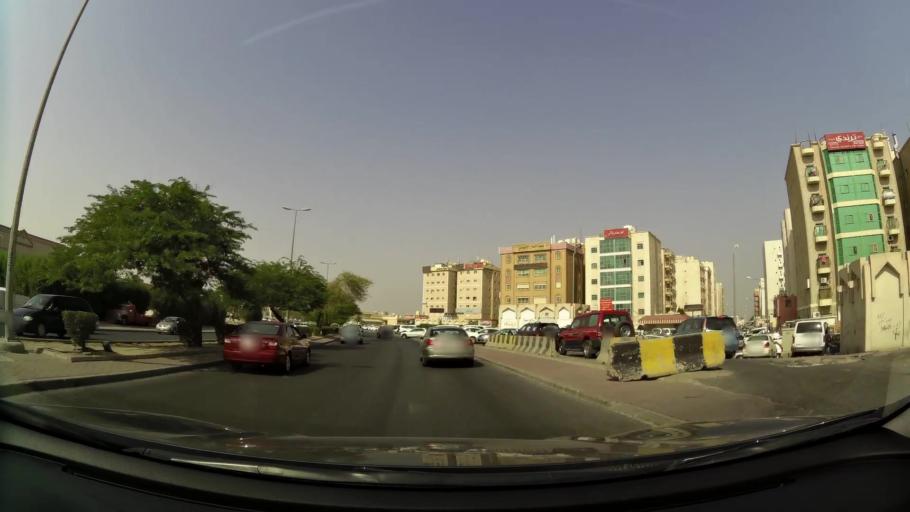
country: KW
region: Muhafazat al Jahra'
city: Al Jahra'
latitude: 29.3404
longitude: 47.6676
